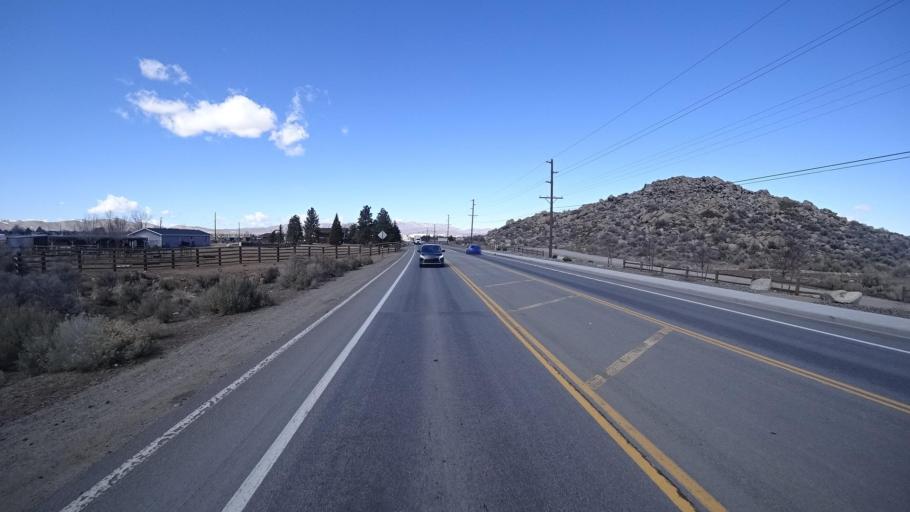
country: US
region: Nevada
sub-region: Washoe County
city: Lemmon Valley
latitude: 39.6325
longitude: -119.8543
